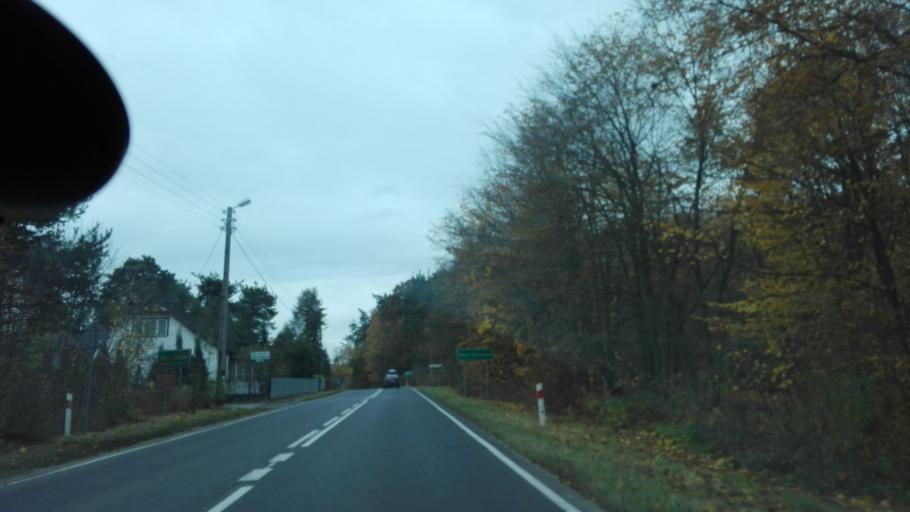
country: PL
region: Lublin Voivodeship
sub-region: Powiat pulawski
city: Pulawy
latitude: 51.4197
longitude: 21.9258
